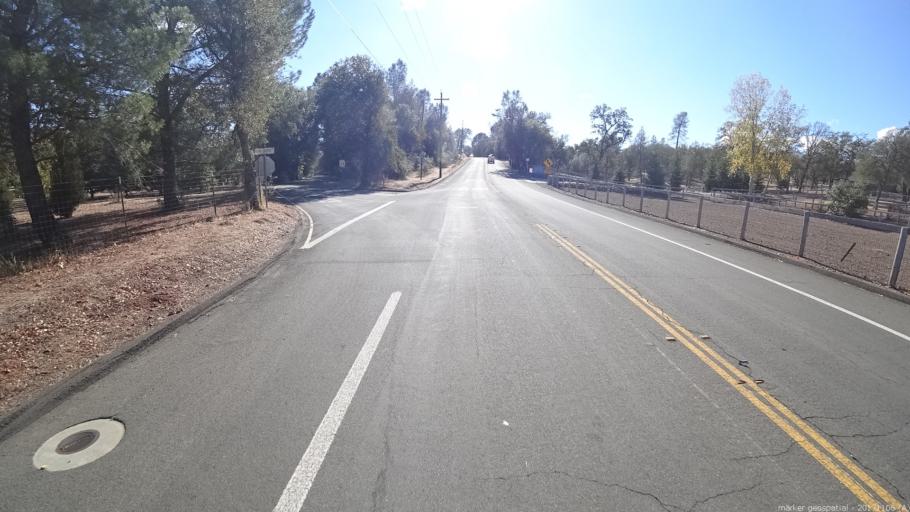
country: US
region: California
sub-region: Shasta County
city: Palo Cedro
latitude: 40.5867
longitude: -122.3064
